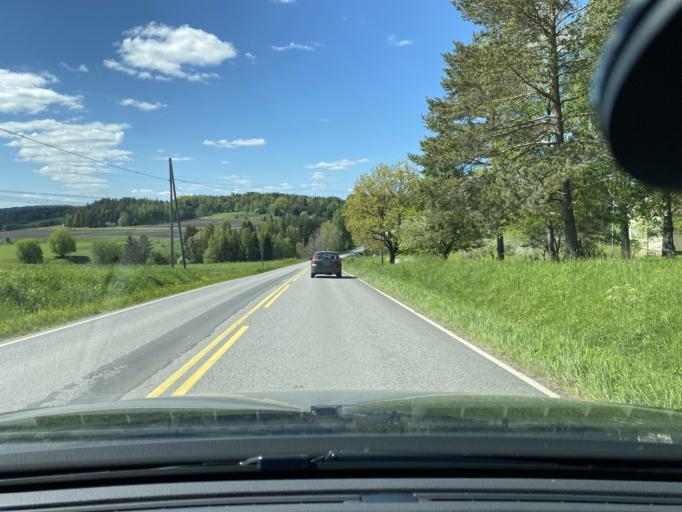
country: FI
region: Varsinais-Suomi
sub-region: Salo
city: Halikko
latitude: 60.3675
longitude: 23.0059
